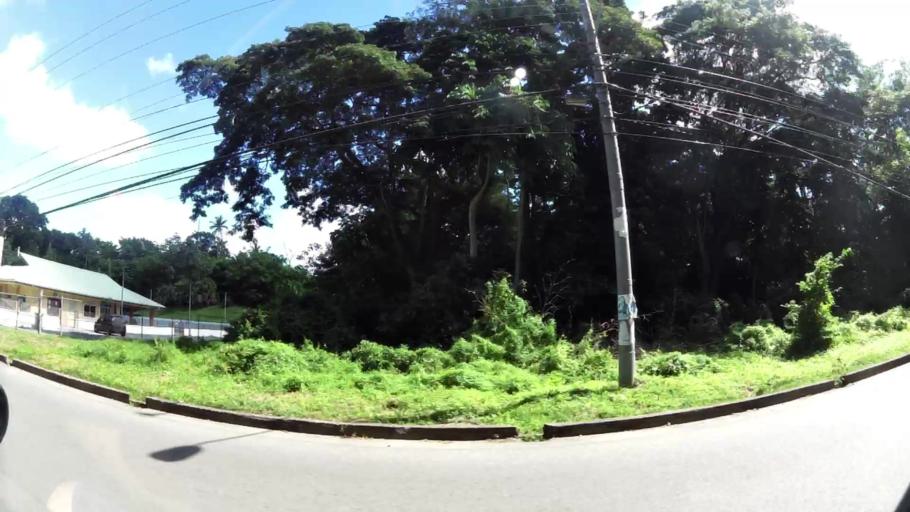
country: TT
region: Tobago
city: Scarborough
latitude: 11.2116
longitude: -60.7790
